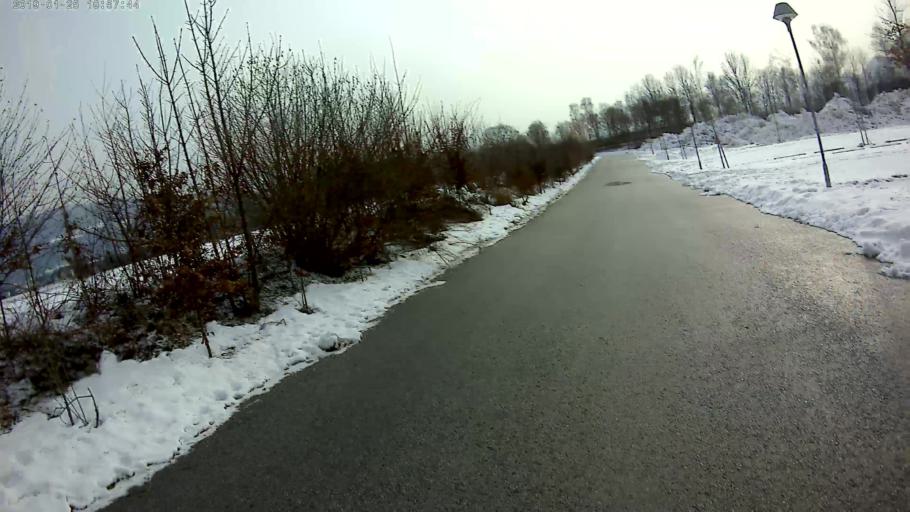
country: AT
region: Salzburg
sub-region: Politischer Bezirk Salzburg-Umgebung
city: Anif
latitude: 47.7420
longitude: 13.0517
